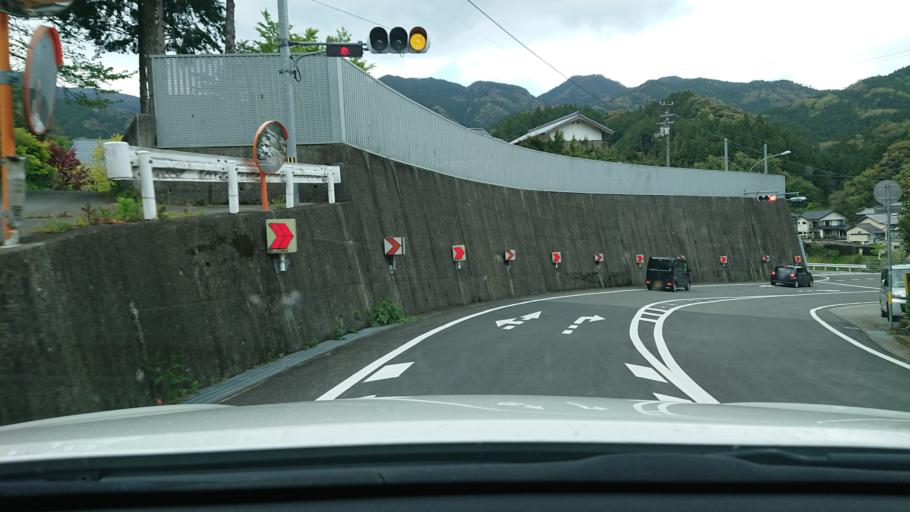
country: JP
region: Tokushima
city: Ishii
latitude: 33.9205
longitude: 134.4260
